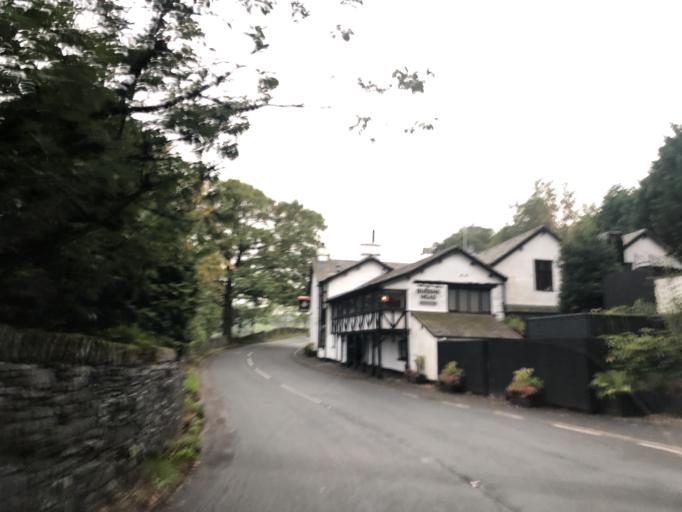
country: GB
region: England
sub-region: Cumbria
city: Windermere
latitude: 54.4265
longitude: -2.9047
